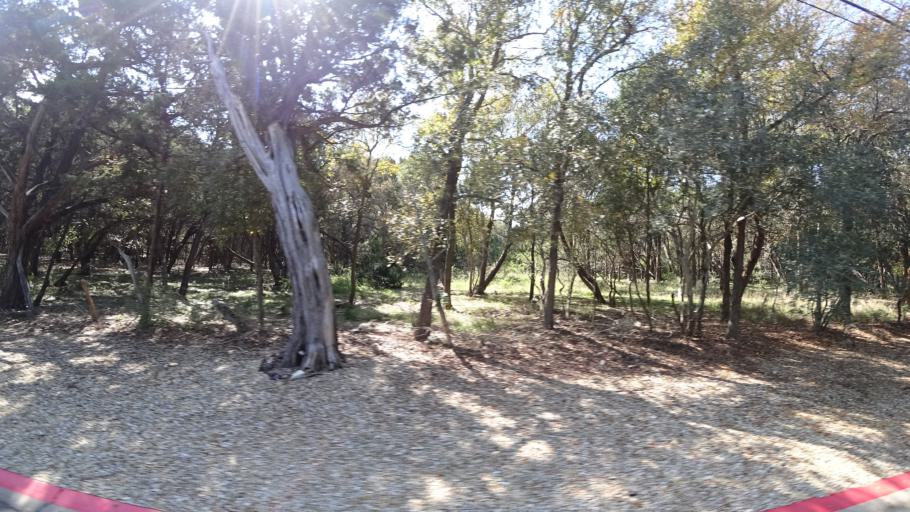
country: US
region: Texas
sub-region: Travis County
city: Shady Hollow
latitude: 30.2109
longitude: -97.8258
